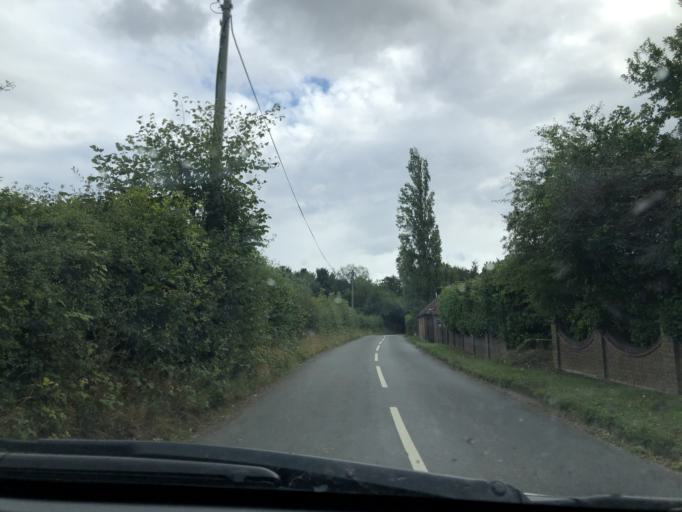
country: GB
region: England
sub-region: Kent
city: Edenbridge
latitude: 51.2269
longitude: 0.0917
